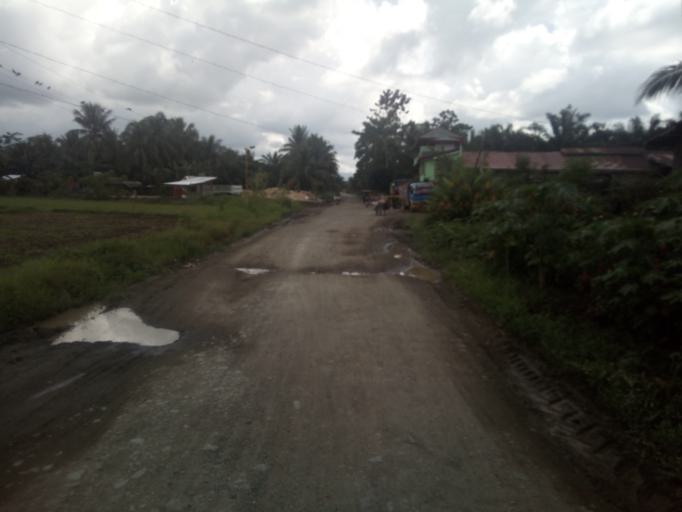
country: PH
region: Caraga
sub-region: Province of Agusan del Sur
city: Santa Josefa
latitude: 7.9971
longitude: 126.0262
